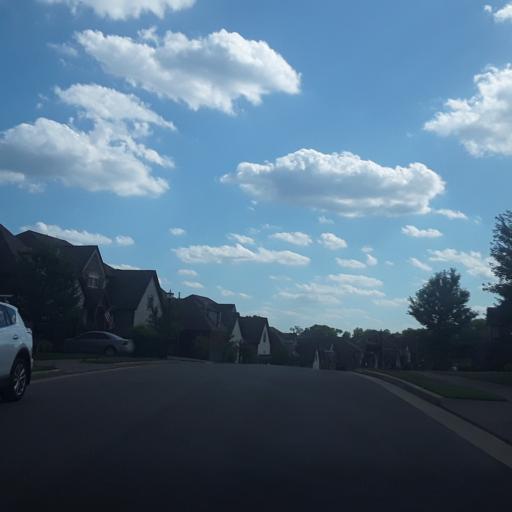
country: US
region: Tennessee
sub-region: Davidson County
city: Lakewood
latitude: 36.1923
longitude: -86.6394
